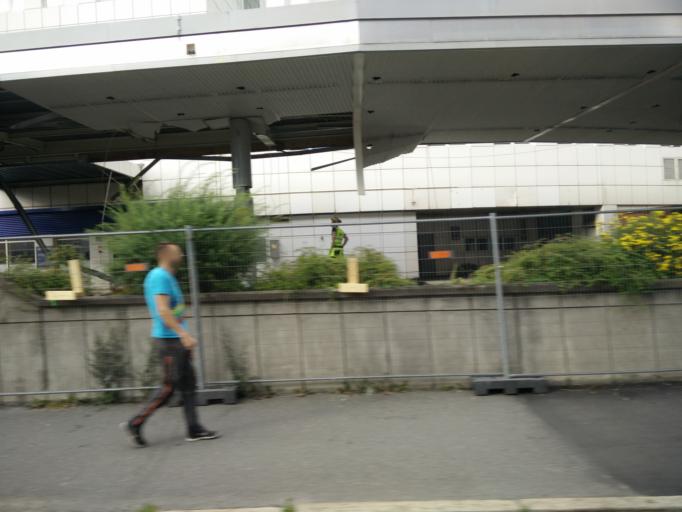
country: NO
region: Oslo
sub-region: Oslo
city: Sjolyststranda
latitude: 59.9307
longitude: 10.7116
